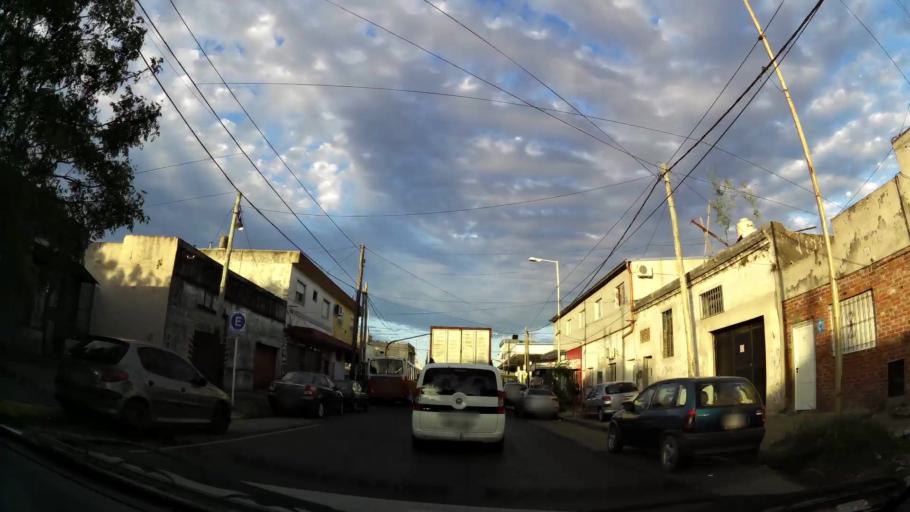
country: AR
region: Buenos Aires
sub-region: Partido de Avellaneda
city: Avellaneda
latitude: -34.7055
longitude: -58.3364
